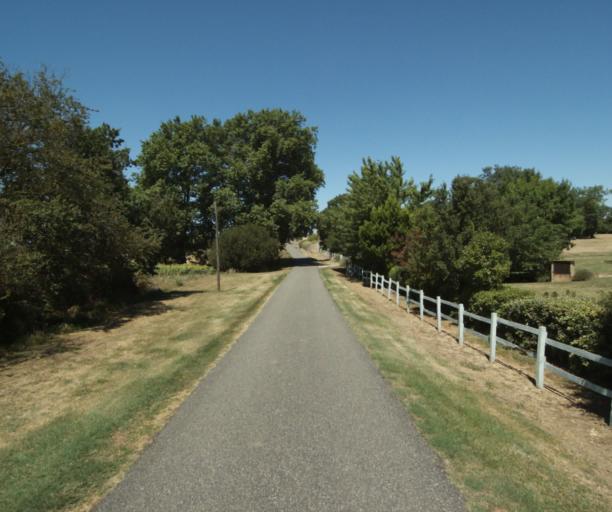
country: FR
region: Midi-Pyrenees
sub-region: Departement de la Haute-Garonne
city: Saint-Felix-Lauragais
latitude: 43.4612
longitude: 1.9051
